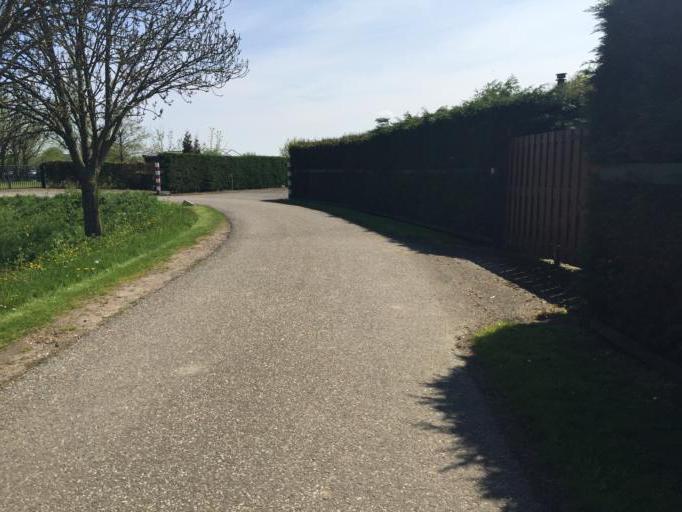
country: NL
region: North Holland
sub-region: Gemeente Aalsmeer
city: Aalsmeer
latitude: 52.2153
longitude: 4.7443
